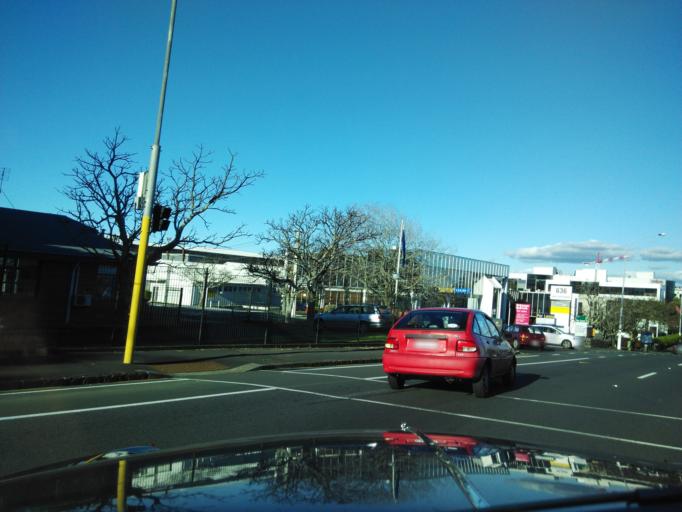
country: NZ
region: Auckland
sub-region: Auckland
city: Auckland
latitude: -36.8995
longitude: 174.8044
